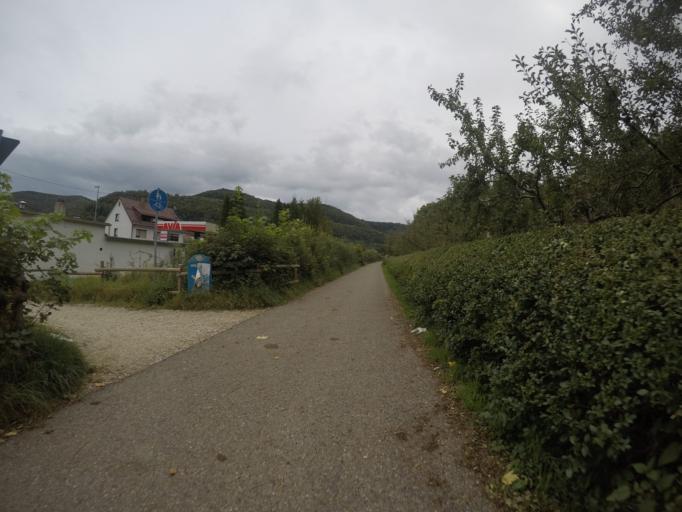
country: DE
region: Baden-Wuerttemberg
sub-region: Tuebingen Region
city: Pfullingen
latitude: 48.4398
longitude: 9.2523
